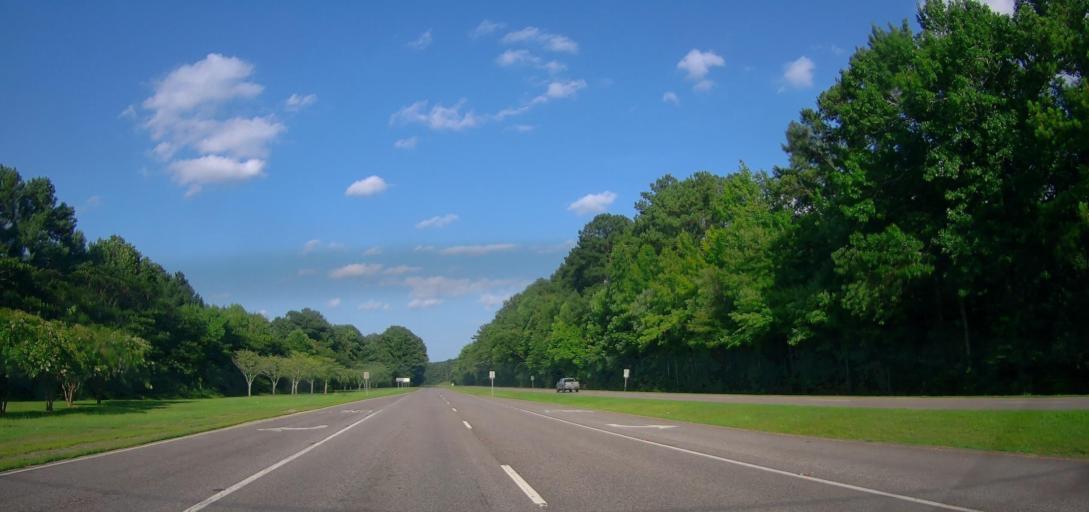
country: US
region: Alabama
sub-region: Jefferson County
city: Irondale
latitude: 33.5467
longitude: -86.6798
